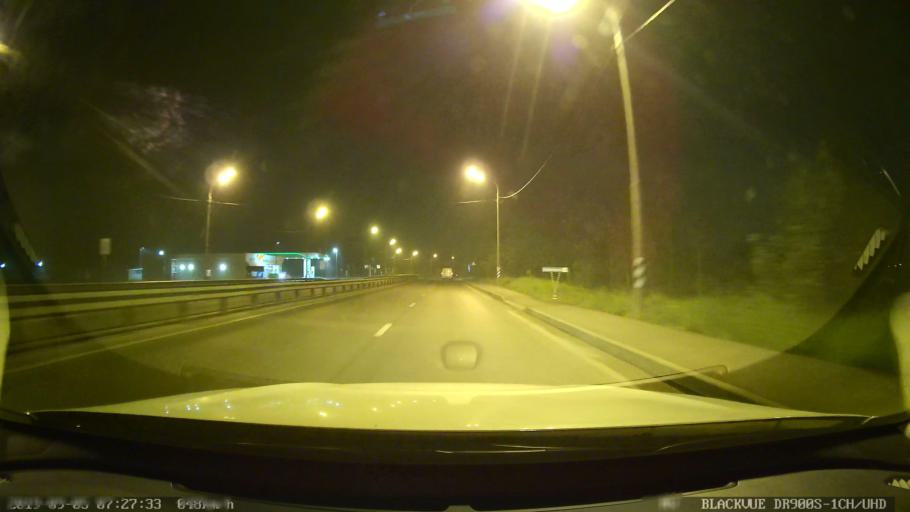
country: RU
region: Moskovskaya
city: Povedniki
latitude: 55.9517
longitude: 37.6513
